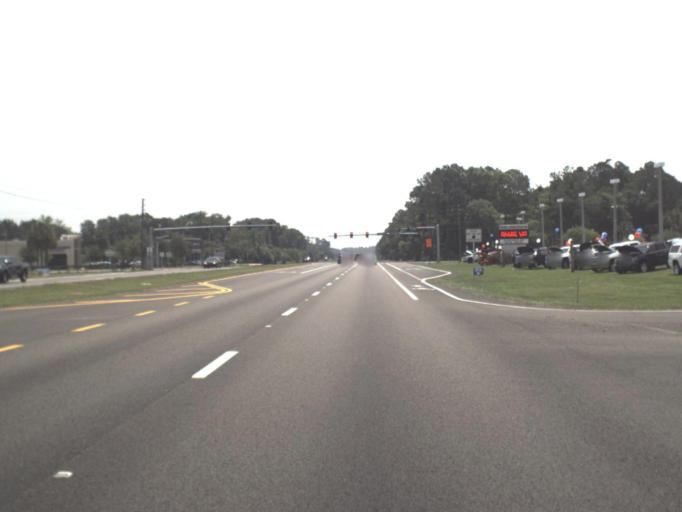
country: US
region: Florida
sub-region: Nassau County
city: Yulee
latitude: 30.6217
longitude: -81.5312
